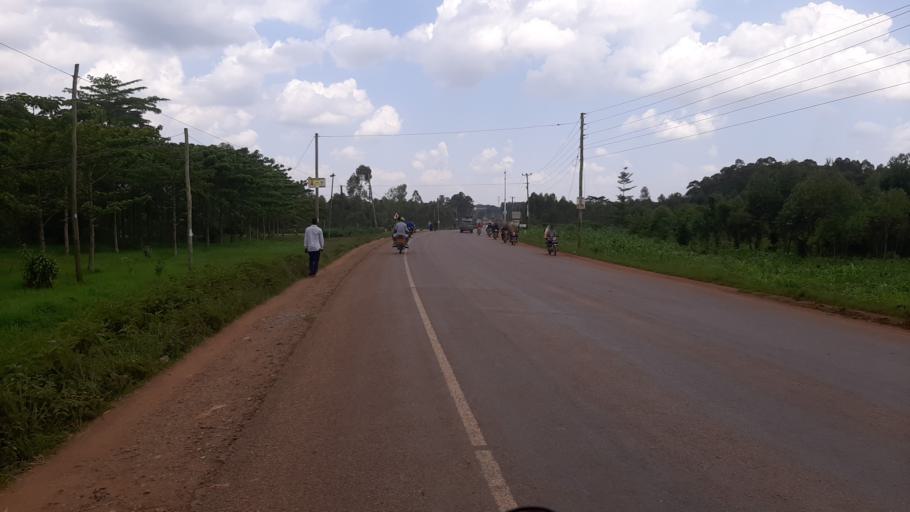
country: UG
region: Eastern Region
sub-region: Mbale District
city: Mbale
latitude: 1.0565
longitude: 34.1801
